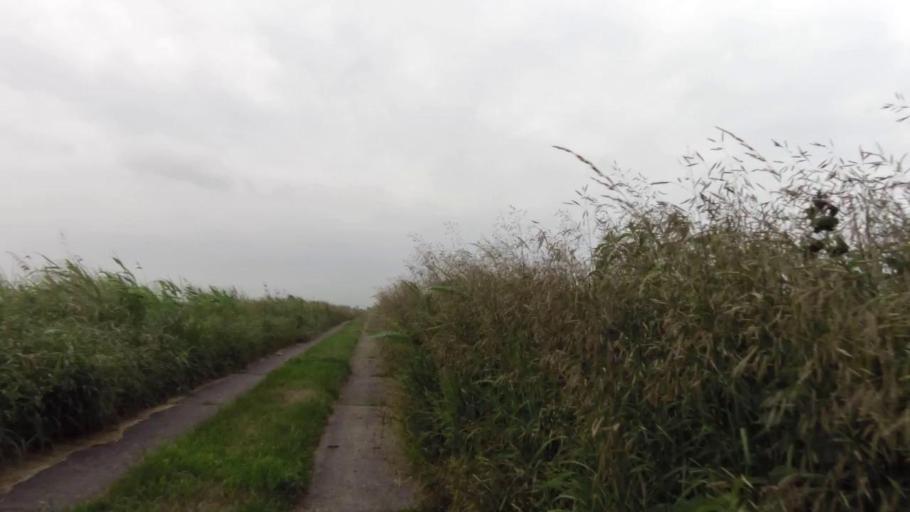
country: PL
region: West Pomeranian Voivodeship
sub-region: Powiat goleniowski
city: Stepnica
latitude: 53.5703
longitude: 14.6956
